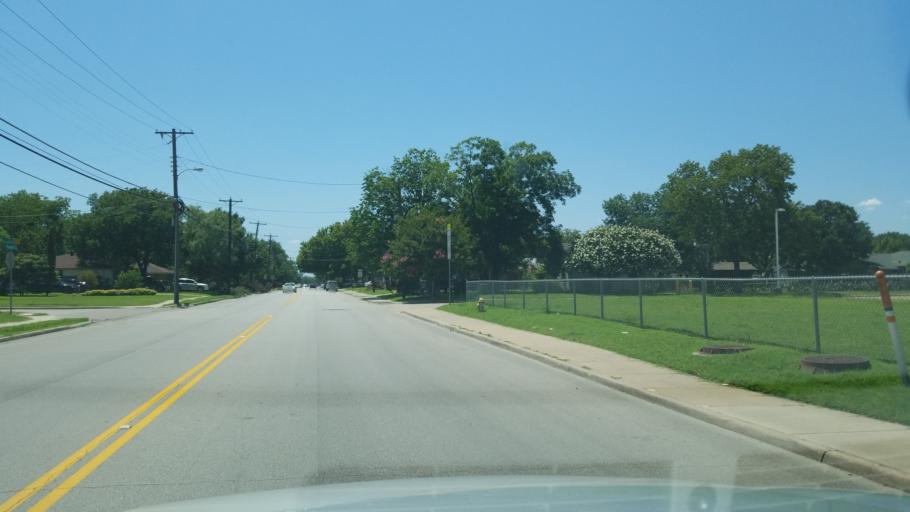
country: US
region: Texas
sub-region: Dallas County
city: Irving
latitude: 32.8176
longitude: -96.9287
